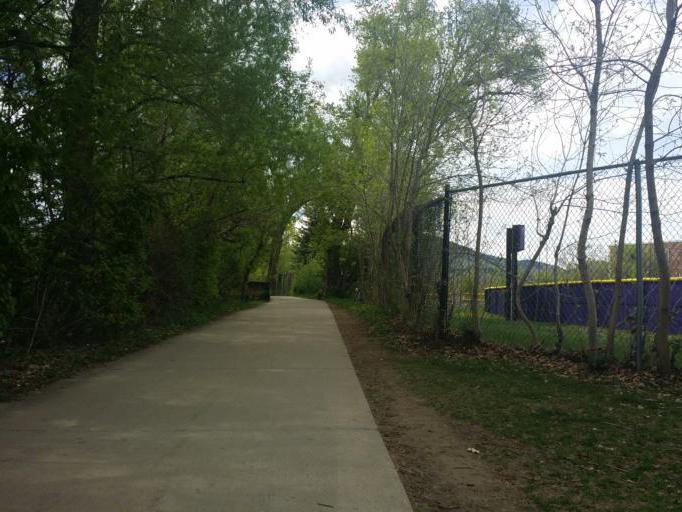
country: US
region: Colorado
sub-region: Boulder County
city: Boulder
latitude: 40.0124
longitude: -105.2733
